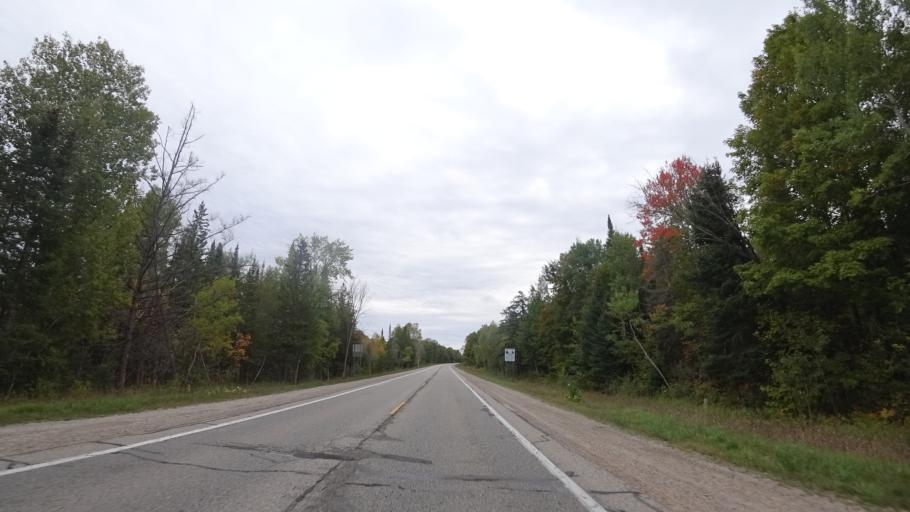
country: US
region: Michigan
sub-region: Charlevoix County
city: Boyne City
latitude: 45.2434
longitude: -84.9179
